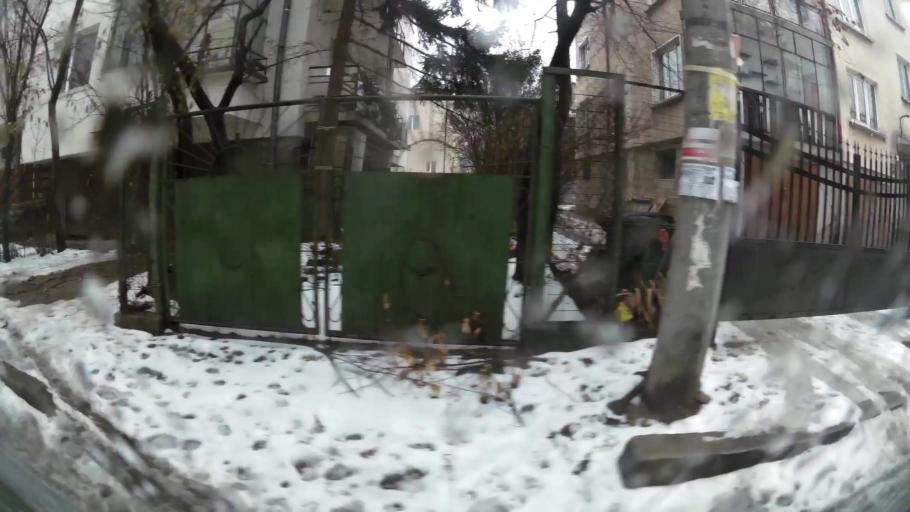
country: BG
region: Sofia-Capital
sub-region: Stolichna Obshtina
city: Sofia
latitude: 42.6806
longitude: 23.2651
